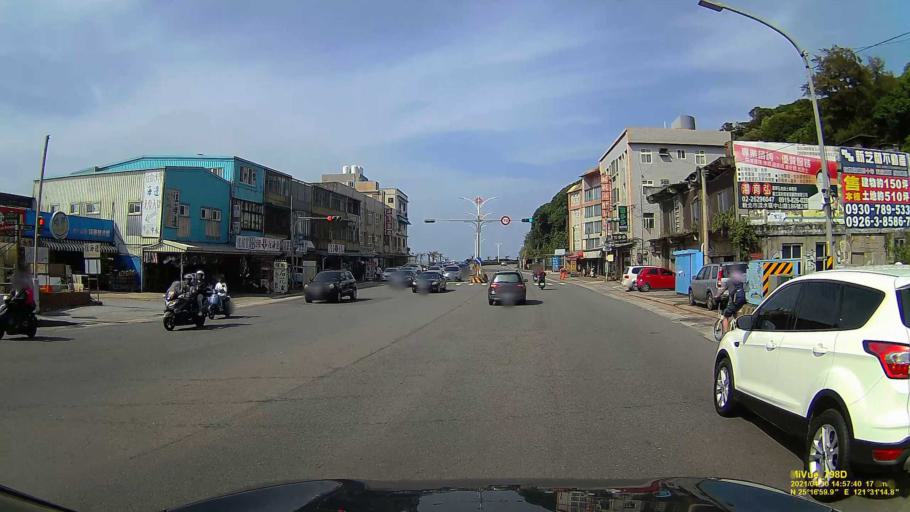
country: TW
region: Taipei
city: Taipei
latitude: 25.2834
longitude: 121.5208
